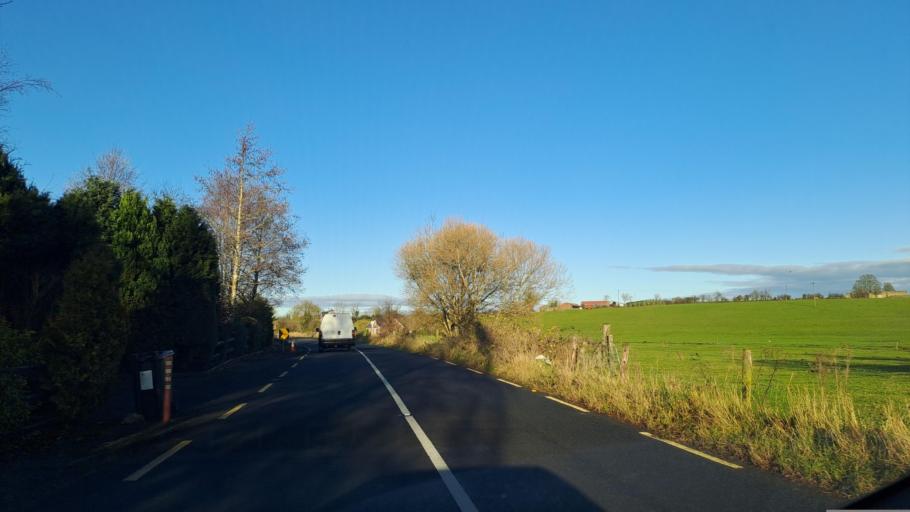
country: IE
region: Ulster
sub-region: An Cabhan
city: Mullagh
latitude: 53.8282
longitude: -6.9522
